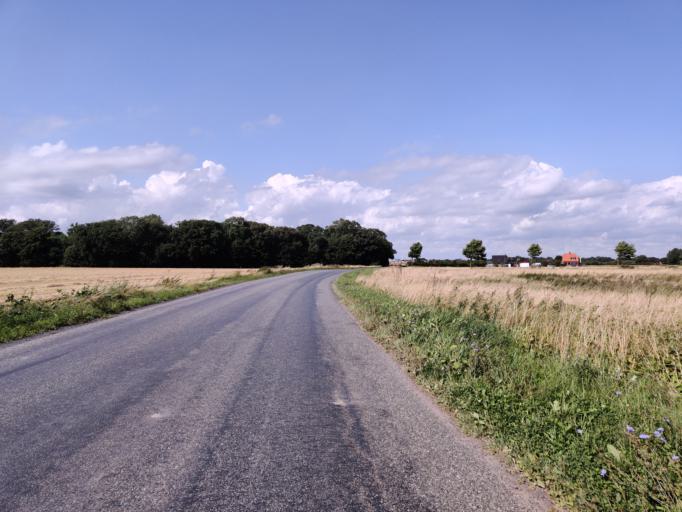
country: DK
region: Zealand
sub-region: Guldborgsund Kommune
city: Nykobing Falster
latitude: 54.6413
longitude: 11.8958
